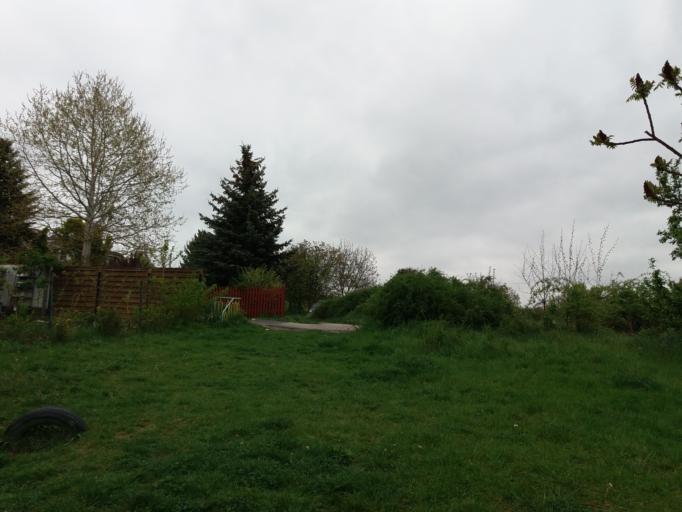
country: HU
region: Pest
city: Pomaz
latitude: 47.6329
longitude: 19.0370
